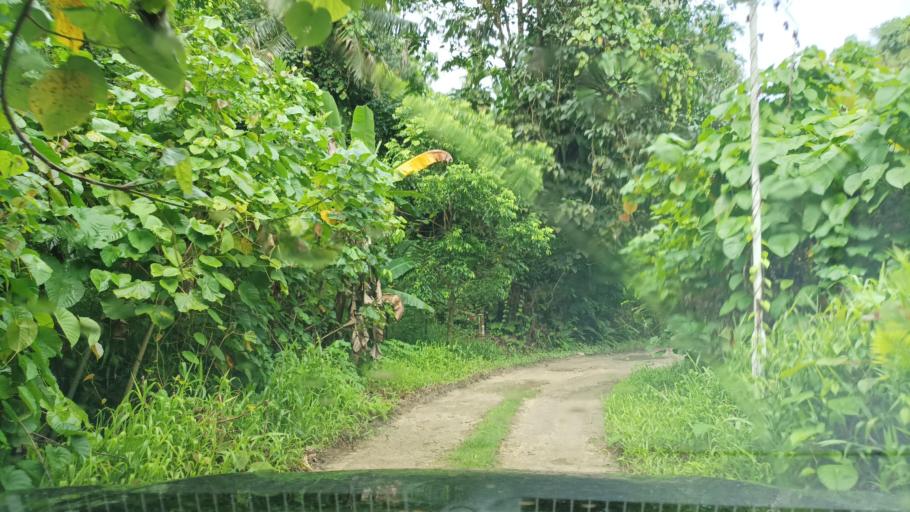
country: FM
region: Pohnpei
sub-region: Madolenihm Municipality
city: Madolenihm Municipality Government
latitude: 6.9158
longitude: 158.2921
